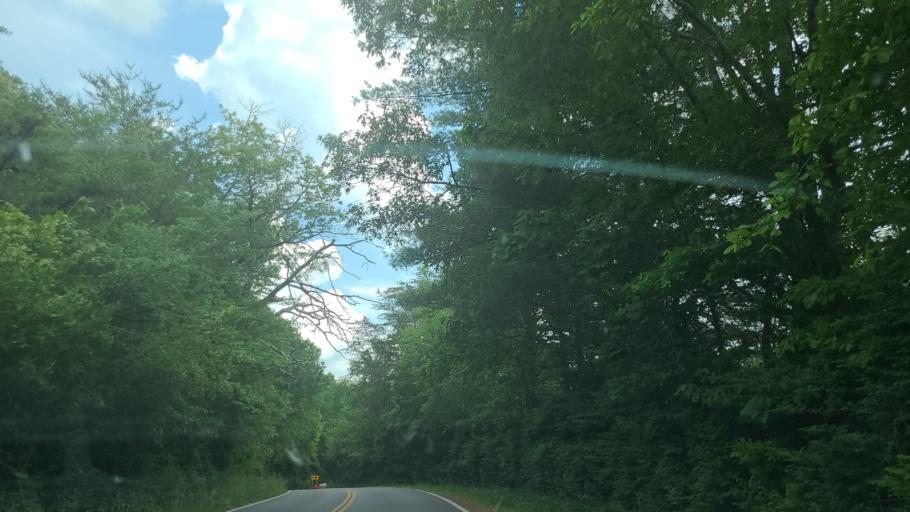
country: US
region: Tennessee
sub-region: Cumberland County
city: Lake Tansi
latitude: 35.8963
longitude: -85.0263
